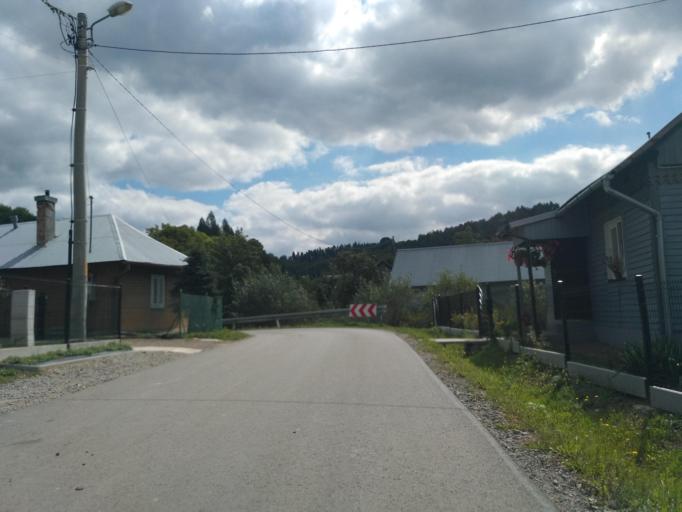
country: PL
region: Subcarpathian Voivodeship
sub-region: Powiat rzeszowski
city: Dynow
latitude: 49.7754
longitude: 22.2412
